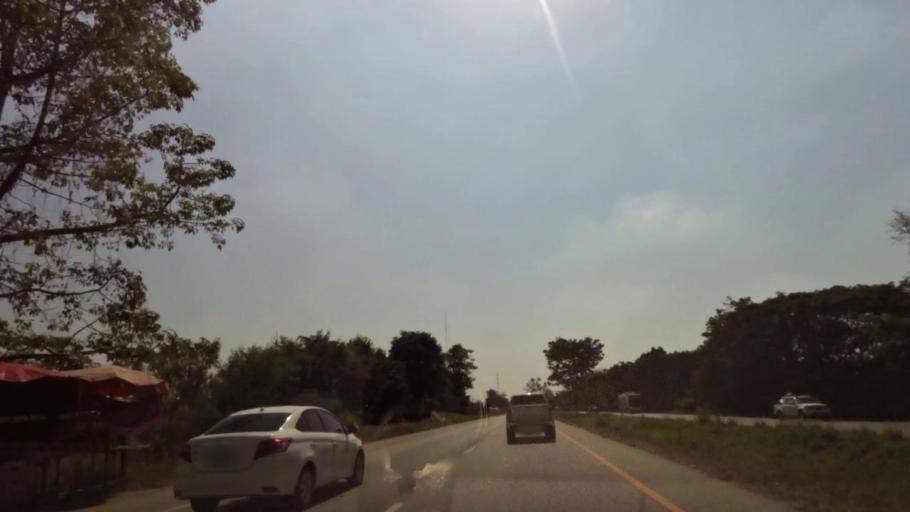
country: TH
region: Phichit
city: Wachira Barami
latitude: 16.4198
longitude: 100.1439
